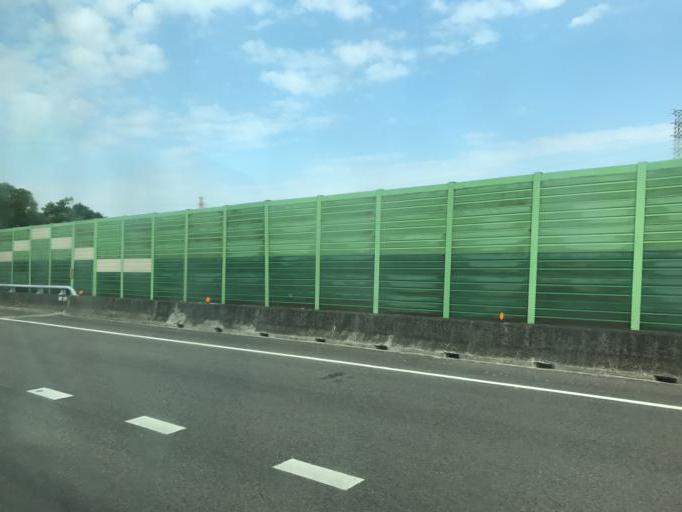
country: TW
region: Taiwan
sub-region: Hsinchu
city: Zhubei
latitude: 24.8037
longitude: 121.0096
